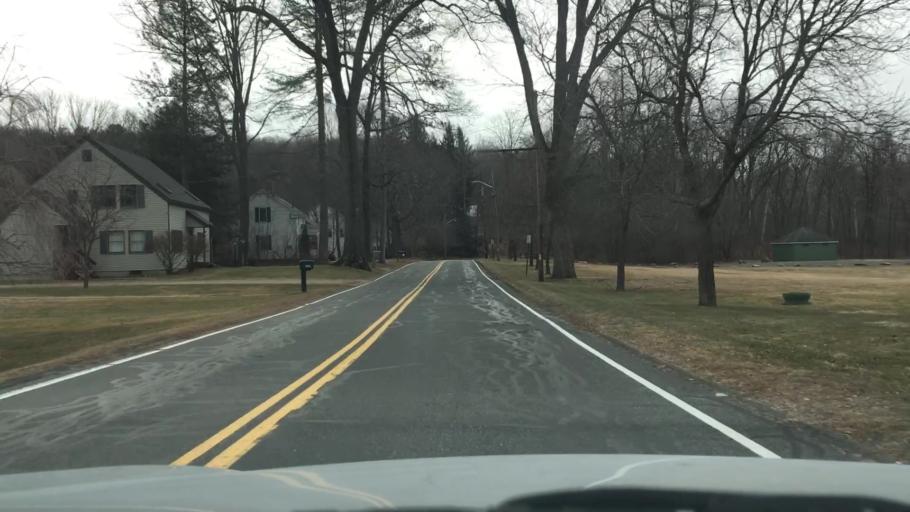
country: US
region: Massachusetts
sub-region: Hampshire County
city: Northampton
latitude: 42.3281
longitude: -72.6700
